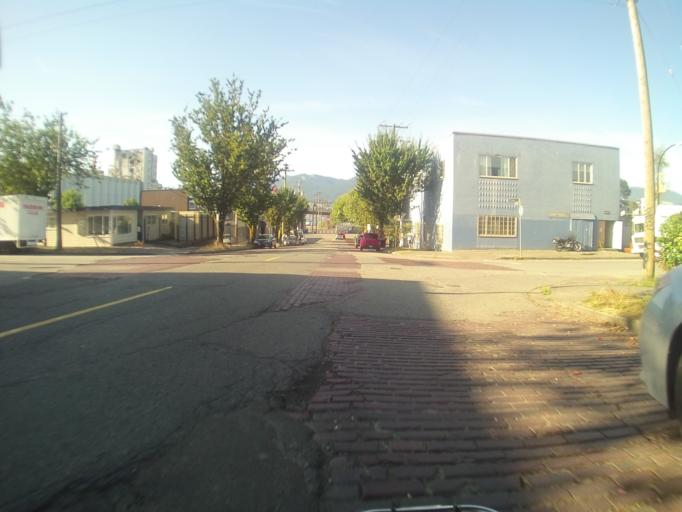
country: CA
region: British Columbia
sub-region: Fraser Valley Regional District
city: North Vancouver
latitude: 49.2838
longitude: -123.0654
